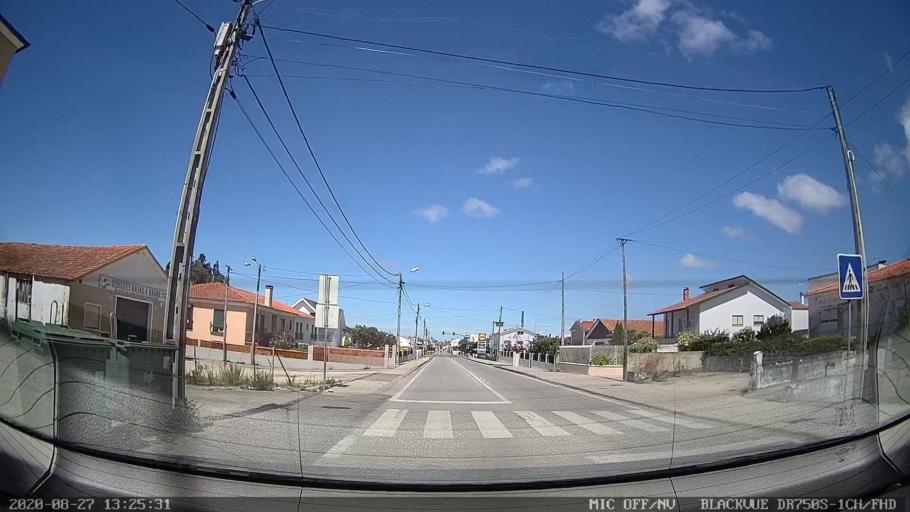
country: PT
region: Aveiro
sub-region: Vagos
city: Vagos
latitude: 40.5459
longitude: -8.6787
